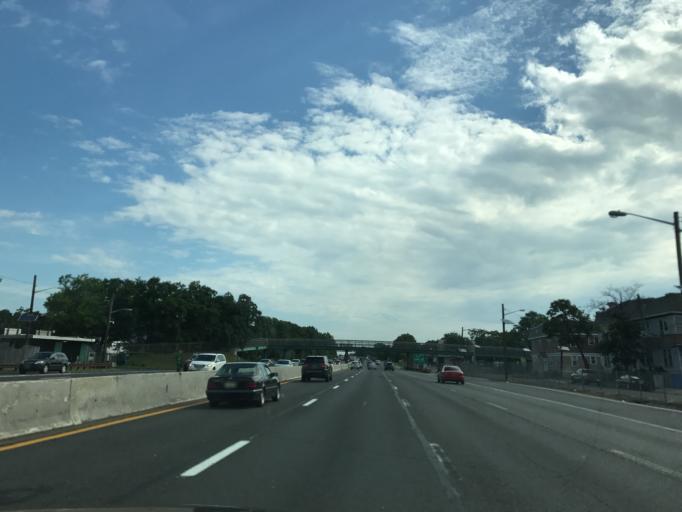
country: US
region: New Jersey
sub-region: Essex County
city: Irvington
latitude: 40.7378
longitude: -74.2175
